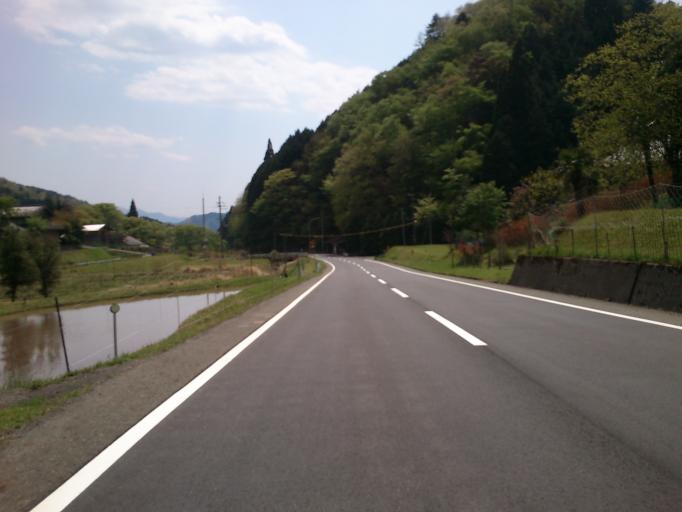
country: JP
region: Hyogo
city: Toyooka
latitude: 35.4011
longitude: 134.9473
